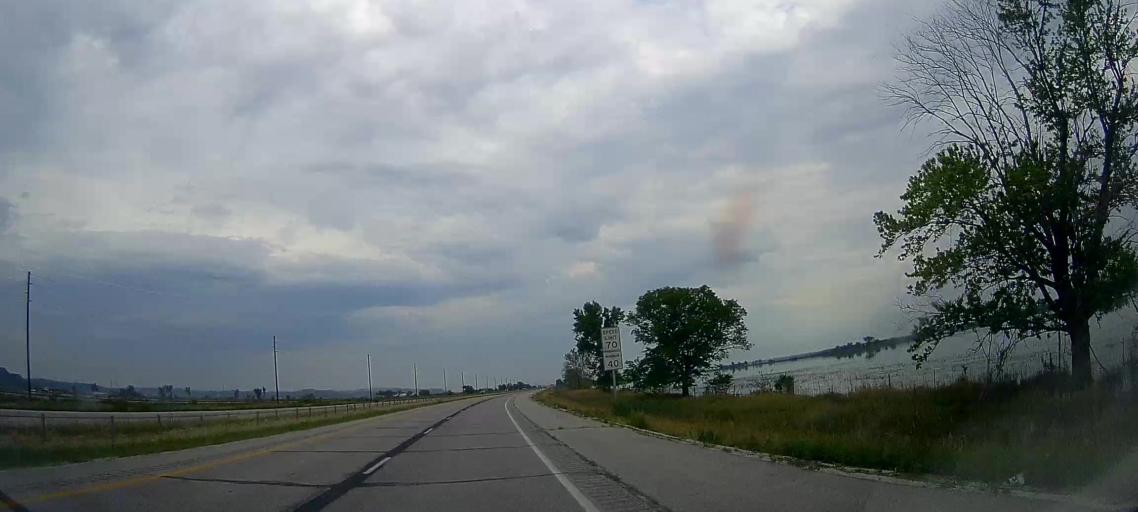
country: US
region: Iowa
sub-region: Pottawattamie County
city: Carter Lake
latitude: 41.4108
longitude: -95.8997
